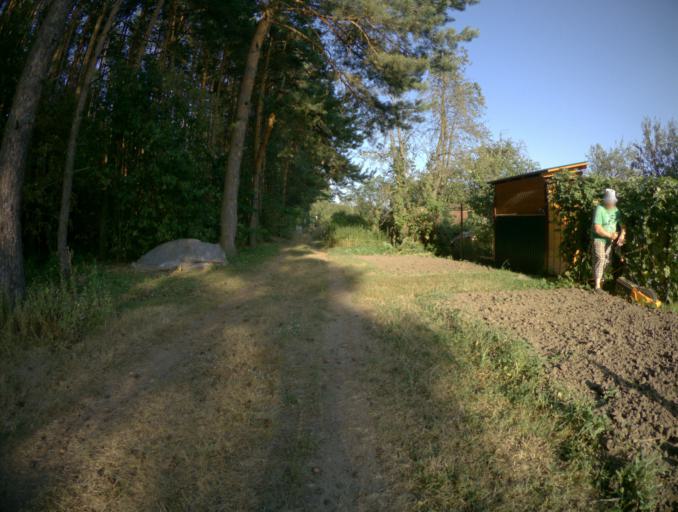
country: RU
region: Vladimir
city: Kommunar
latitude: 56.0521
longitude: 40.4406
